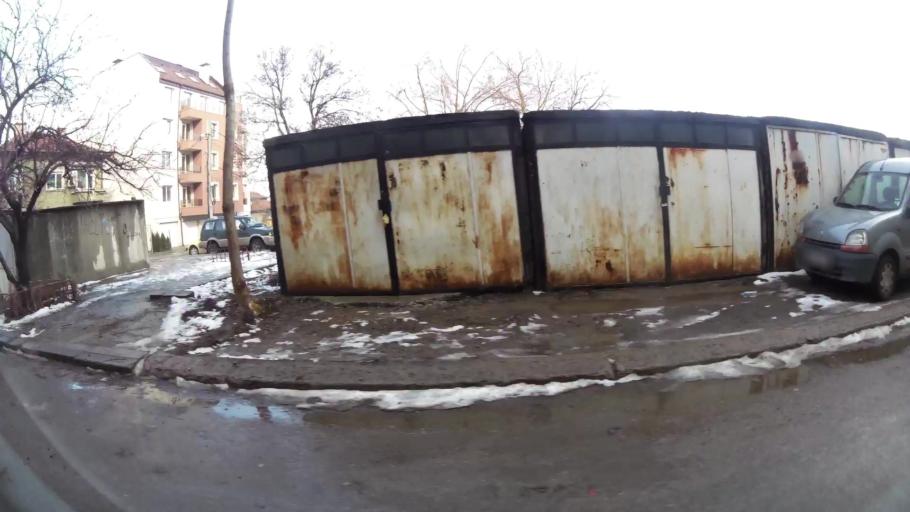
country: BG
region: Sofia-Capital
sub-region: Stolichna Obshtina
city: Sofia
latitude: 42.7201
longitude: 23.2692
